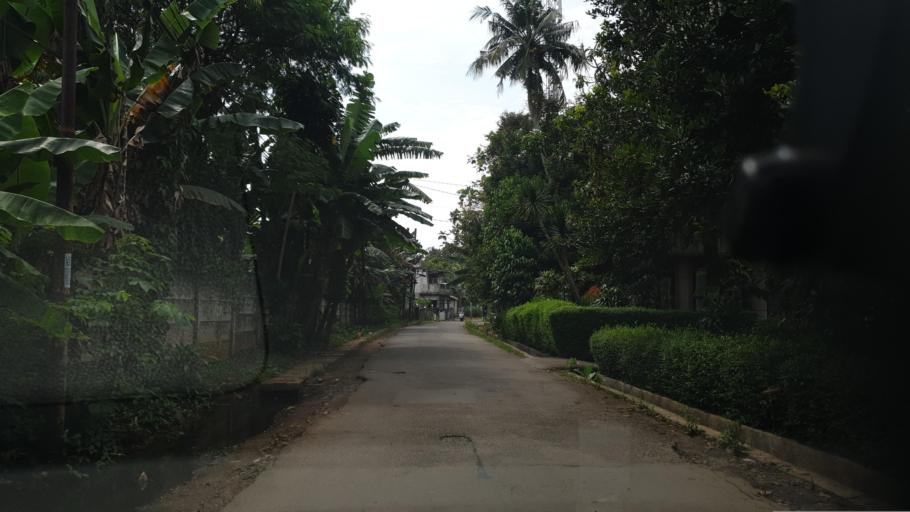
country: ID
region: West Java
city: Pamulang
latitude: -6.3505
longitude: 106.7672
